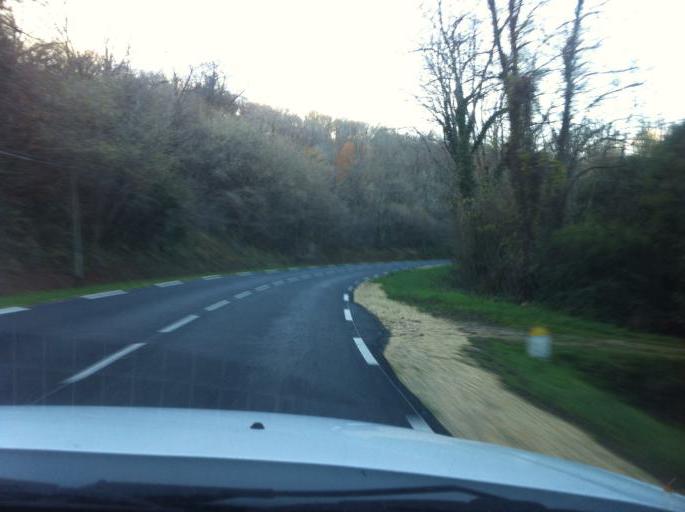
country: FR
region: Aquitaine
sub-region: Departement de la Dordogne
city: Sarlat-la-Caneda
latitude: 44.9100
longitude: 1.1449
